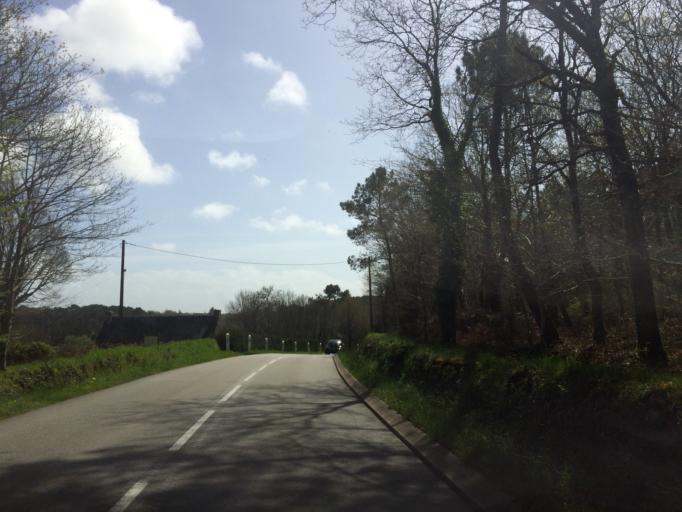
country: FR
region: Brittany
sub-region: Departement du Morbihan
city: Ploemel
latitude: 47.6336
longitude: -3.0476
